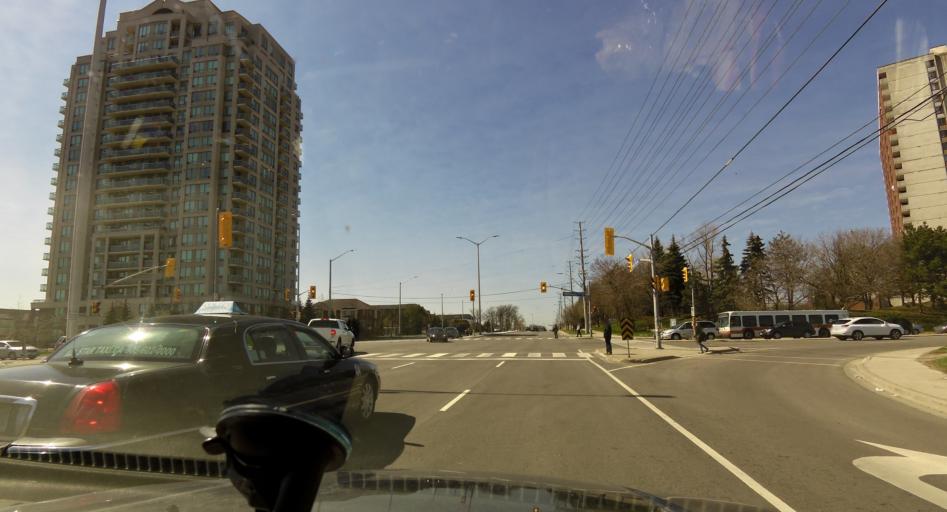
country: CA
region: Ontario
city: Etobicoke
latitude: 43.6259
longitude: -79.6070
